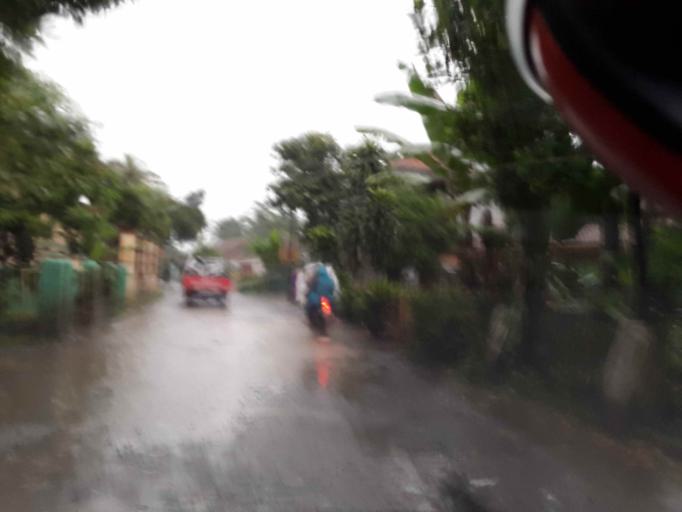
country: ID
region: West Java
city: Padalarang
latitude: -6.9093
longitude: 107.4708
